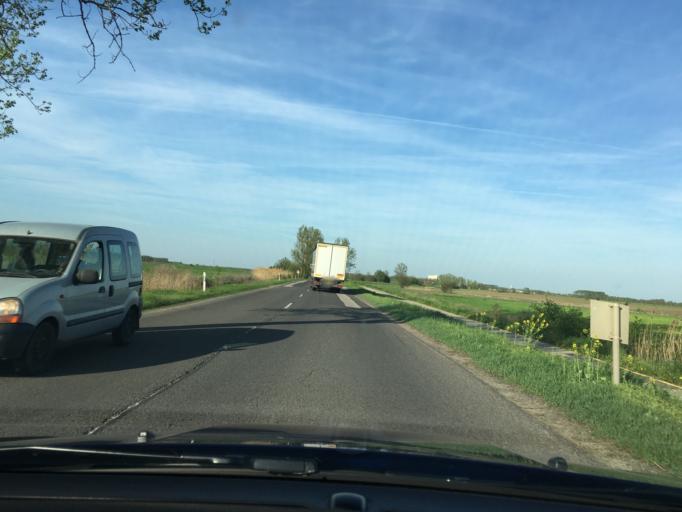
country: HU
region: Bekes
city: Korosladany
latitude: 47.0012
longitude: 21.1153
